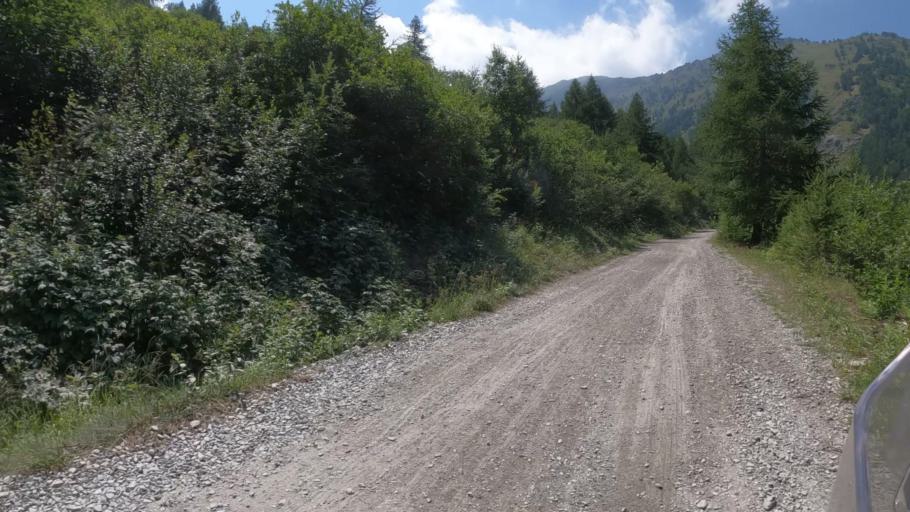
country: IT
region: Piedmont
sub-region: Provincia di Torino
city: Meana di Susa
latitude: 45.0903
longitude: 7.0638
